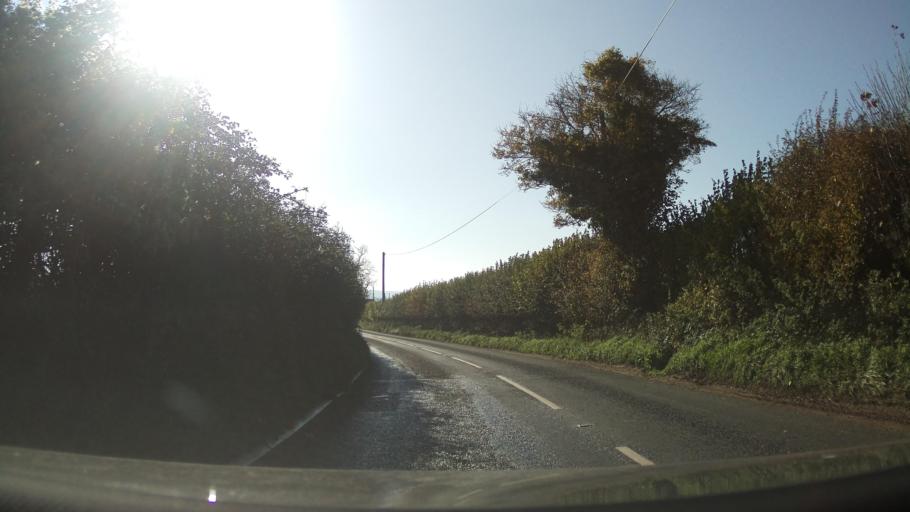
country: GB
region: England
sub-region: Somerset
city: Bruton
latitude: 51.1400
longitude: -2.4279
